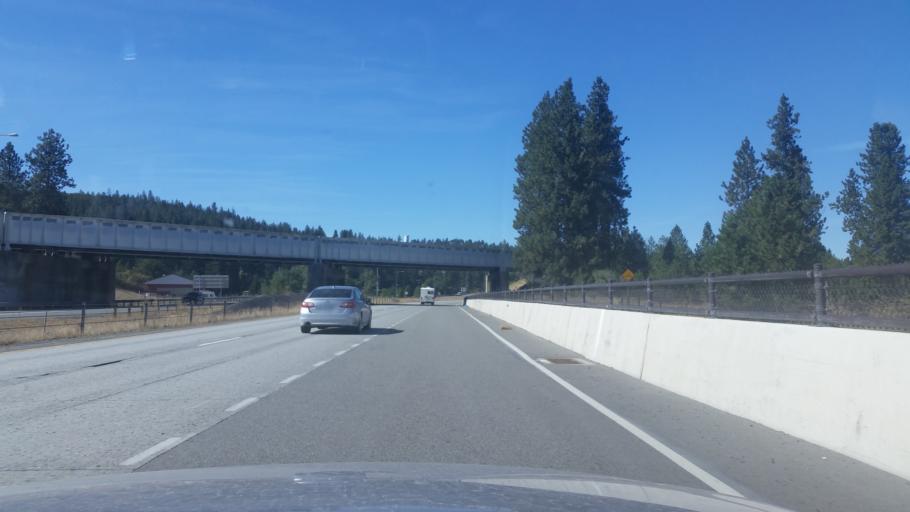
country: US
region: Washington
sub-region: Spokane County
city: Spokane
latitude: 47.6218
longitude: -117.4359
